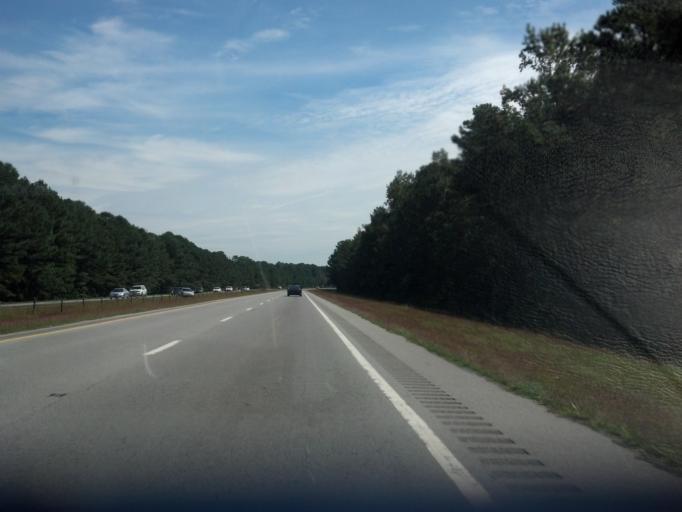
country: US
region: North Carolina
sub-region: Pitt County
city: Summerfield
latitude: 35.6087
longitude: -77.4555
